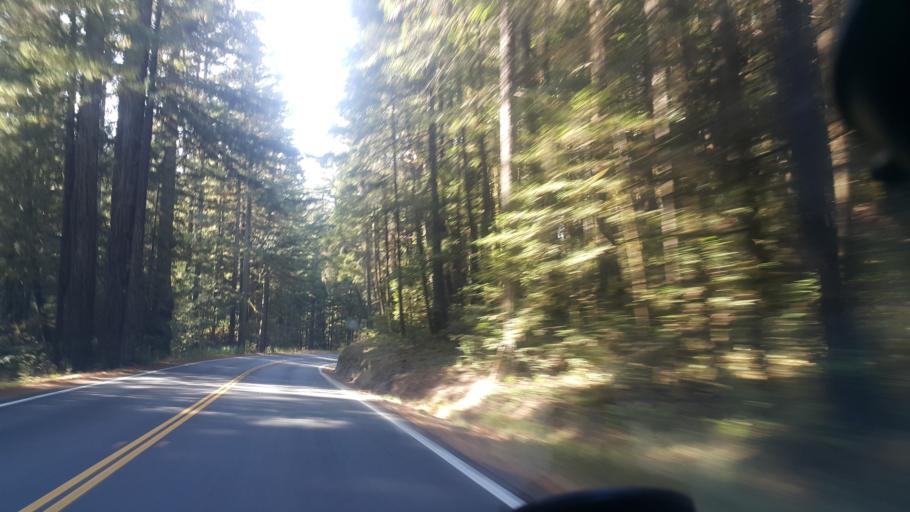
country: US
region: California
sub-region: Mendocino County
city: Brooktrails
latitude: 39.3484
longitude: -123.5621
